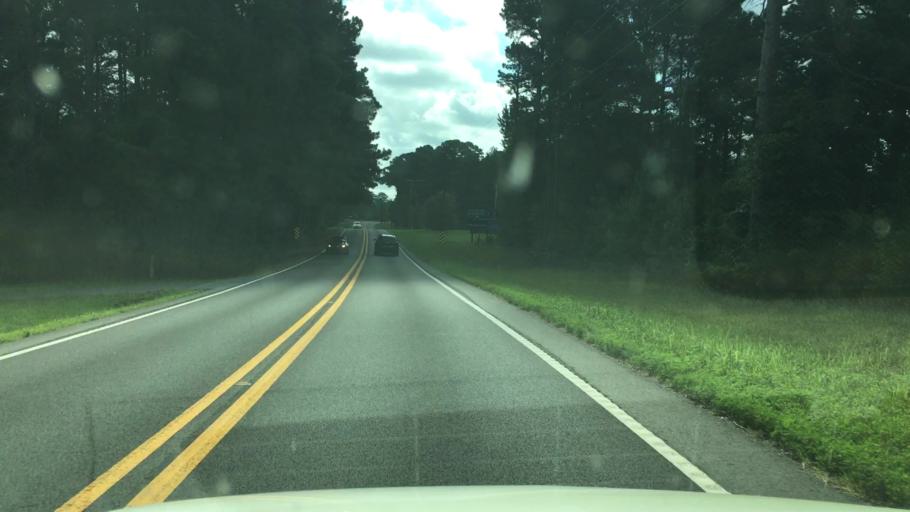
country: US
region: Arkansas
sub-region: Garland County
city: Lake Hamilton
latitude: 34.2787
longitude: -93.1566
